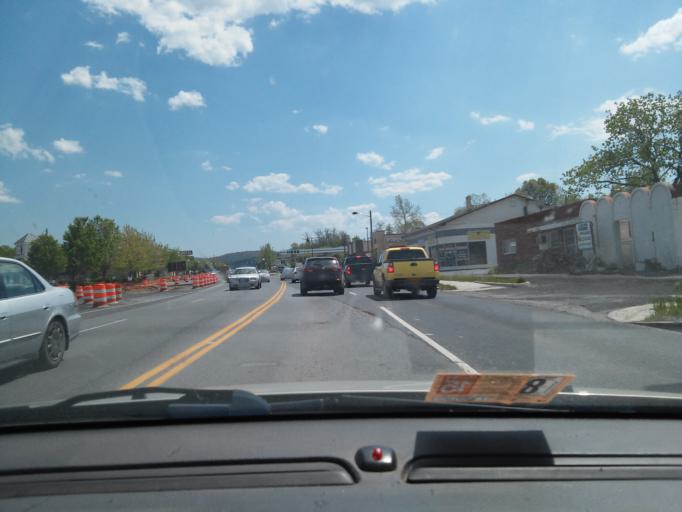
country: US
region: Virginia
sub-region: Warren County
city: Front Royal
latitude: 38.9391
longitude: -78.1994
